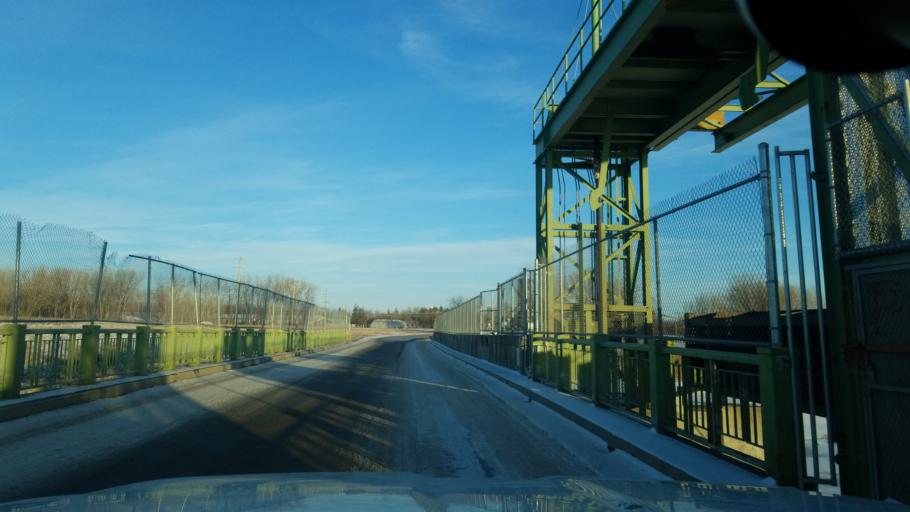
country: CA
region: Manitoba
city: Portage la Prairie
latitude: 49.9493
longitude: -98.3364
